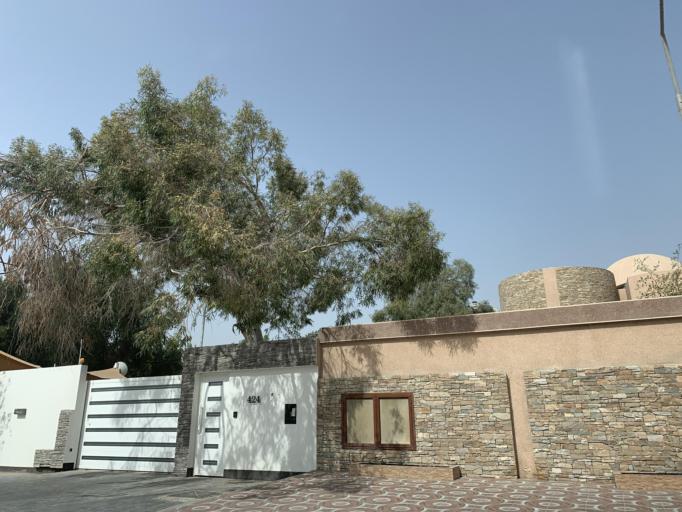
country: BH
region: Northern
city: Madinat `Isa
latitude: 26.1751
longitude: 50.5230
